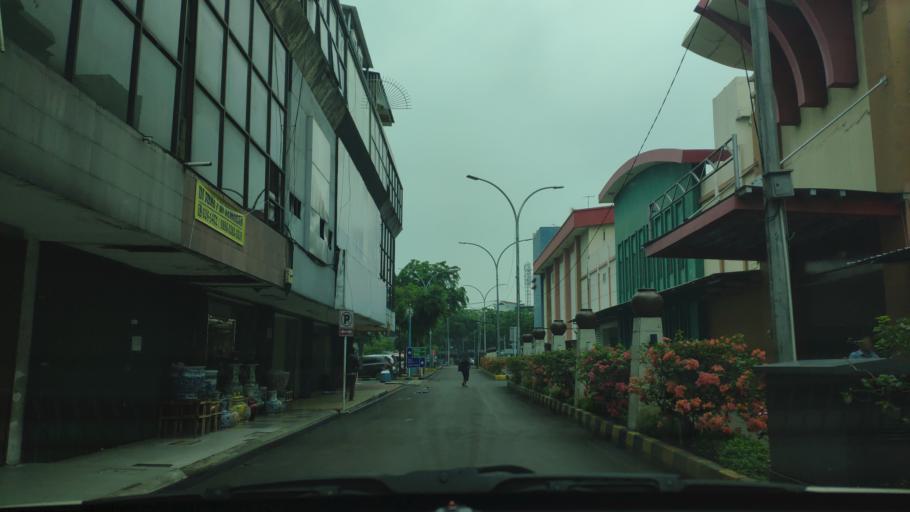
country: ID
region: Jakarta Raya
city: Jakarta
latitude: -6.1658
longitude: 106.8197
